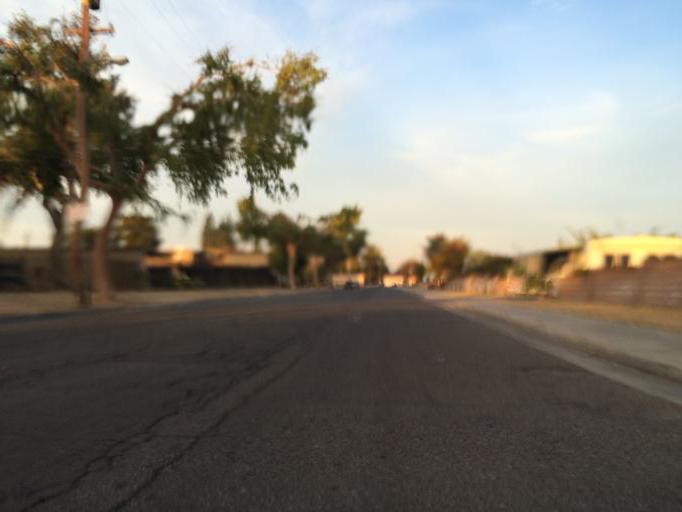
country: US
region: California
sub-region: Fresno County
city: Fresno
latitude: 36.7814
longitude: -119.7613
